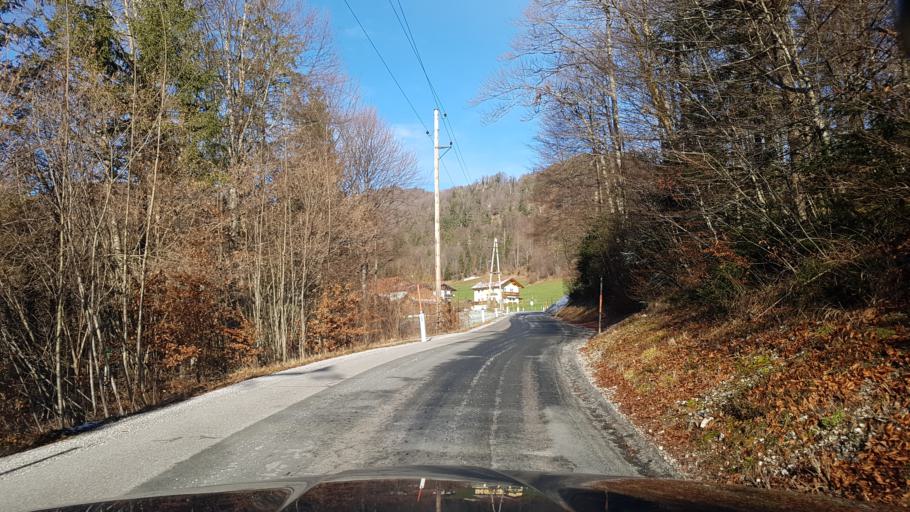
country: AT
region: Salzburg
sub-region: Politischer Bezirk Salzburg-Umgebung
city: Ebenau
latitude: 47.7694
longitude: 13.1727
